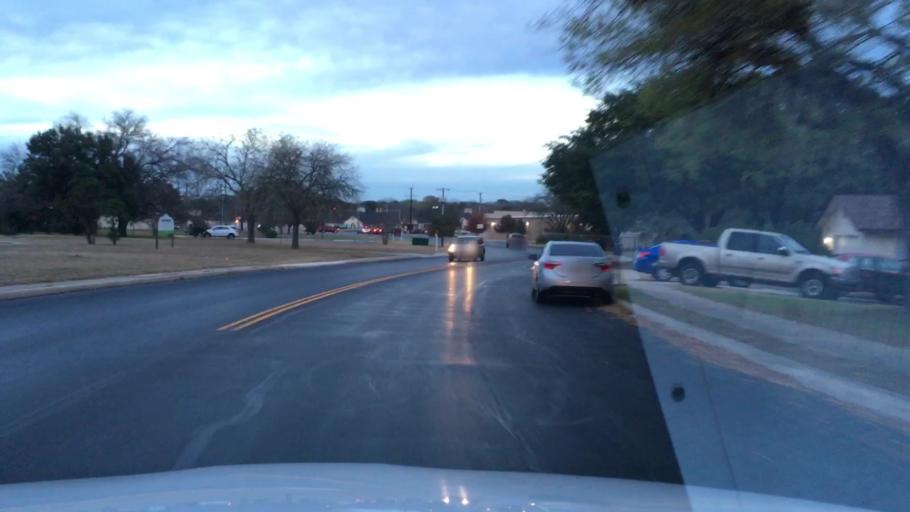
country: US
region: Texas
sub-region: Bexar County
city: Windcrest
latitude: 29.5196
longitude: -98.3552
